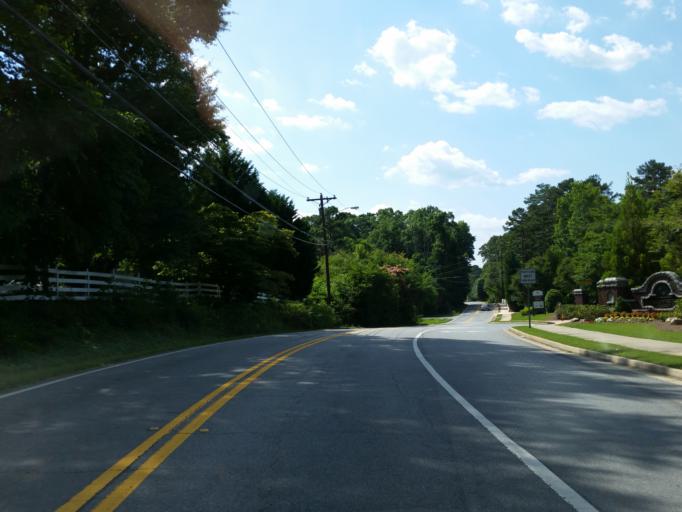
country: US
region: Georgia
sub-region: Cherokee County
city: Woodstock
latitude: 34.0335
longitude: -84.5034
